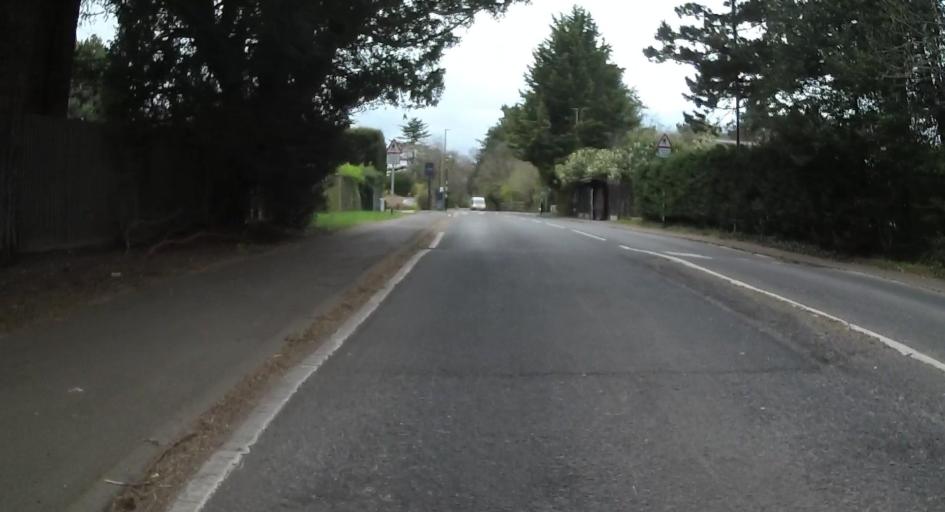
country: GB
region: England
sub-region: Surrey
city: West Byfleet
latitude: 51.3450
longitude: -0.5117
